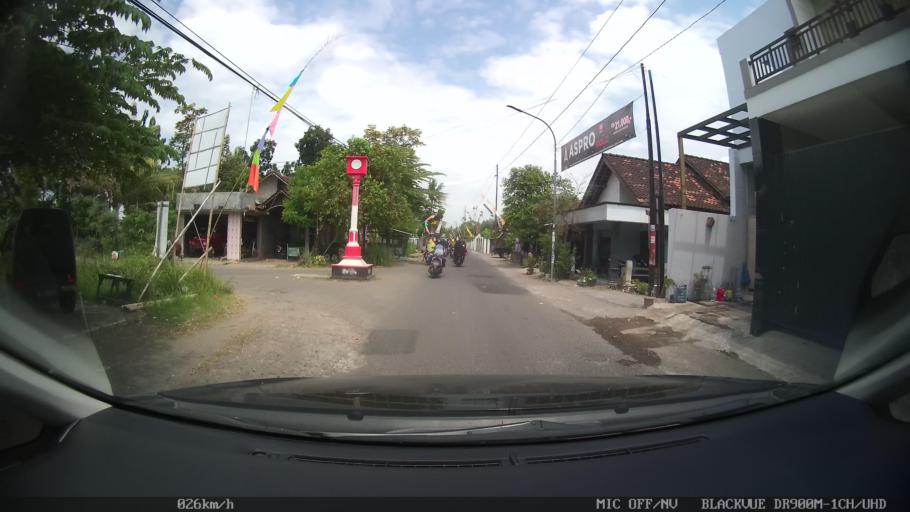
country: ID
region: Central Java
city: Candi Prambanan
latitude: -7.7761
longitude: 110.4778
